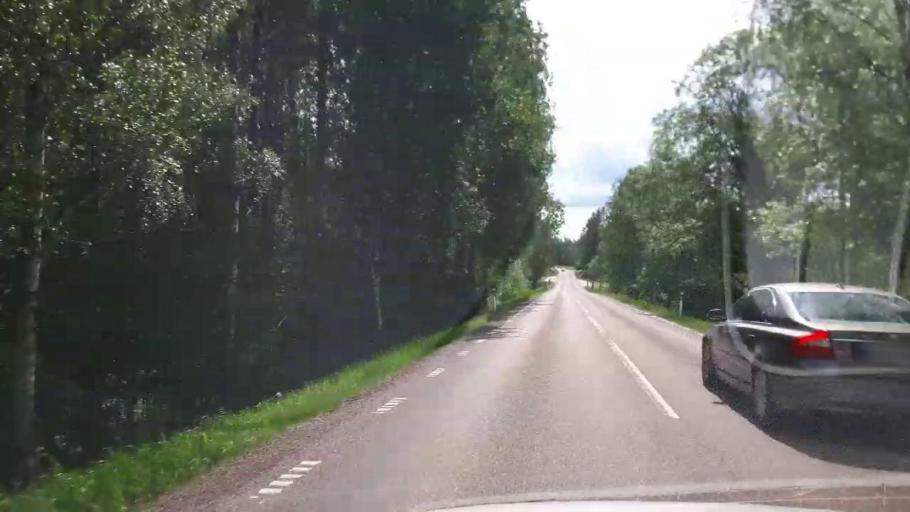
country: SE
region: Dalarna
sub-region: Saters Kommun
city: Saeter
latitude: 60.4192
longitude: 15.8471
